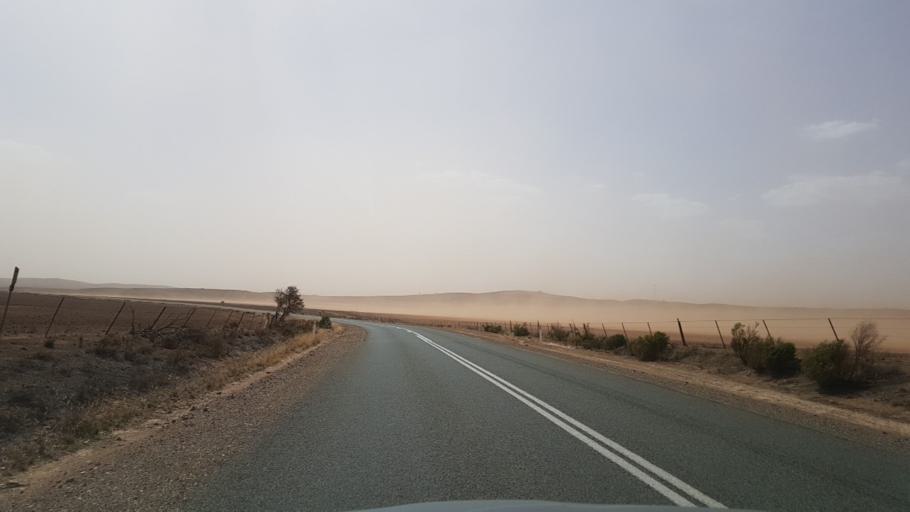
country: AU
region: South Australia
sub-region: Peterborough
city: Peterborough
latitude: -33.1046
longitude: 138.9255
